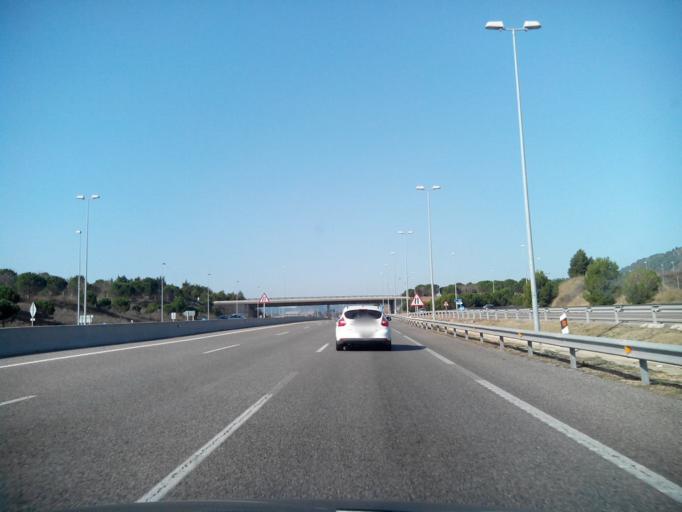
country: ES
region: Catalonia
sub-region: Provincia de Barcelona
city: Jorba
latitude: 41.5944
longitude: 1.5790
